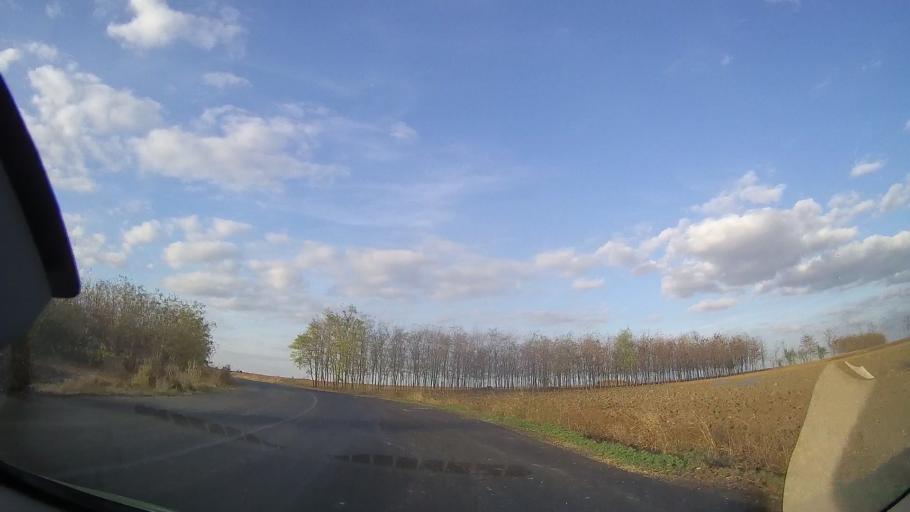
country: RO
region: Constanta
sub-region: Comuna Dumbraveni
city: Dumbraveni
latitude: 43.9280
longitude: 28.0298
